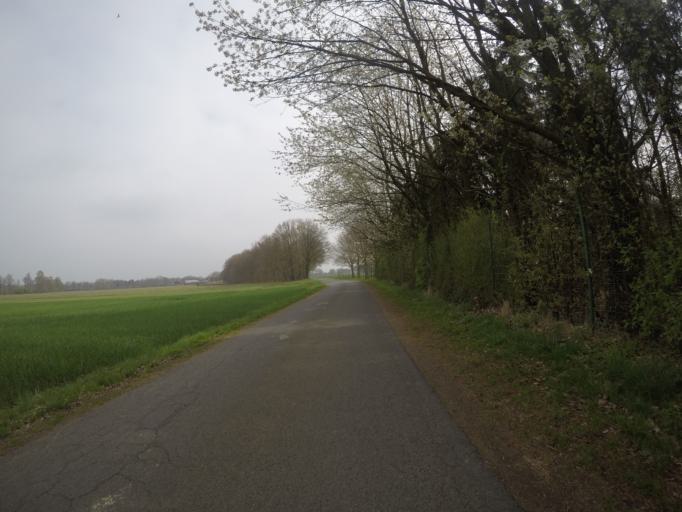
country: DE
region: North Rhine-Westphalia
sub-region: Regierungsbezirk Munster
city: Isselburg
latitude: 51.8685
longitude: 6.5198
